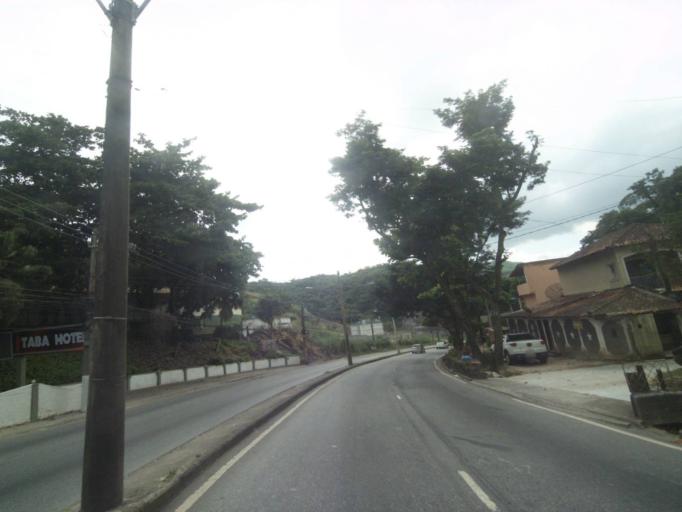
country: BR
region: Rio de Janeiro
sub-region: Nilopolis
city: Nilopolis
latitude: -22.8992
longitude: -43.3961
